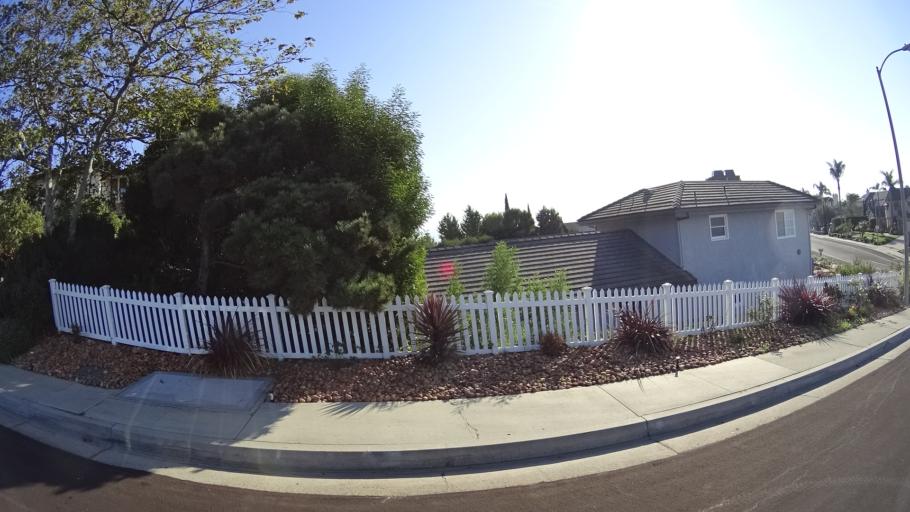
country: US
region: California
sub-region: Orange County
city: San Clemente
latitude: 33.4255
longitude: -117.5955
